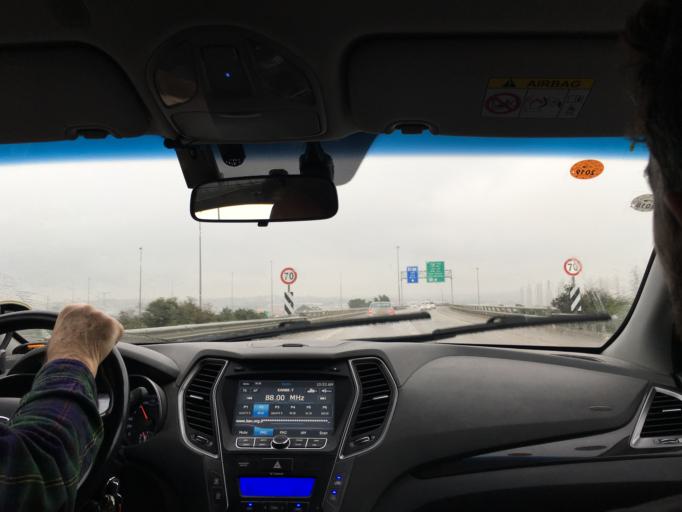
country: IL
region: Central District
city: Rosh Ha'Ayin
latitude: 32.1153
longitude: 34.9347
